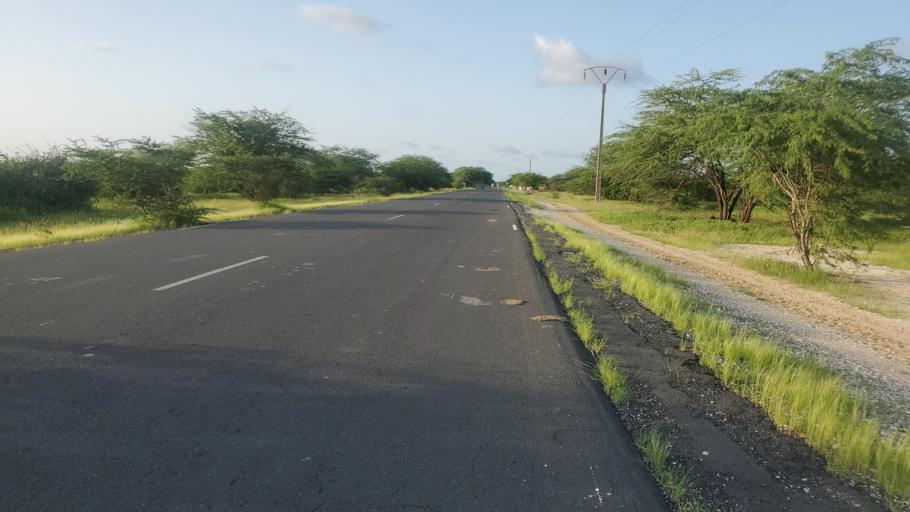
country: SN
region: Saint-Louis
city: Saint-Louis
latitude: 16.1847
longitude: -16.4094
